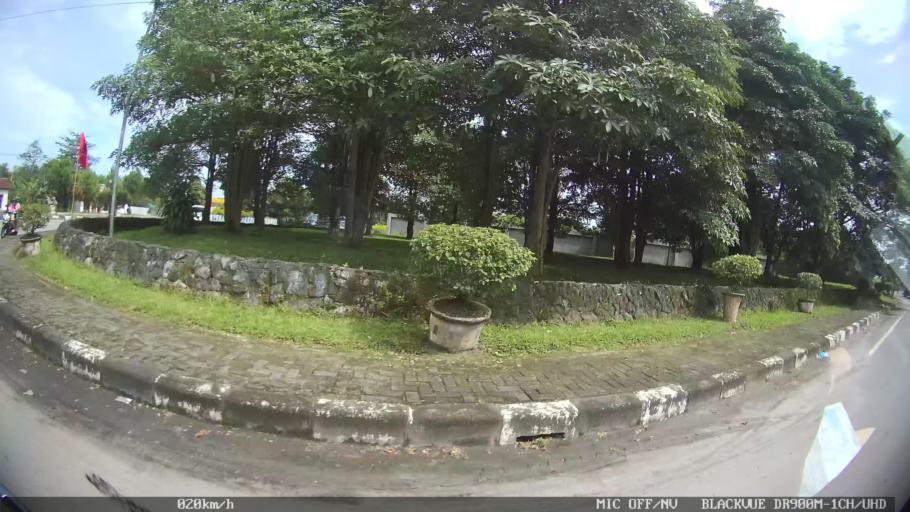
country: ID
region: North Sumatra
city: Percut
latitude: 3.5959
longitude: 98.8075
